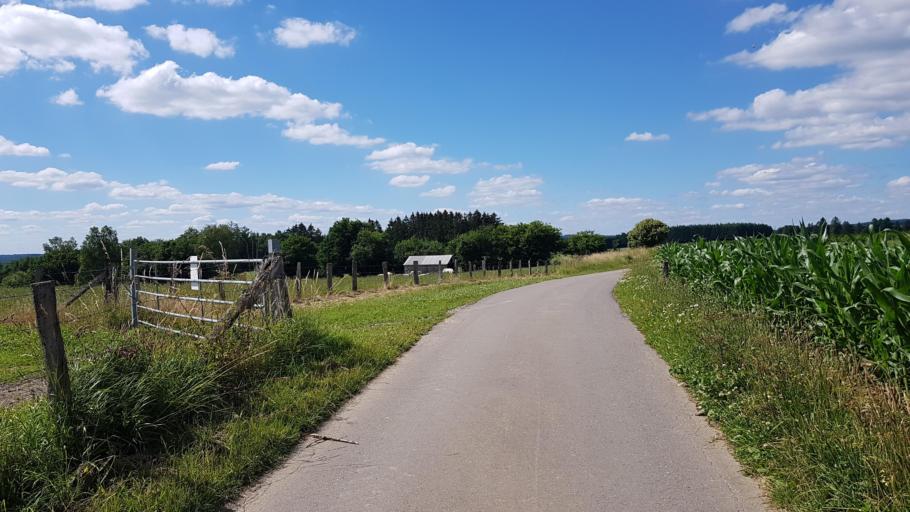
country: BE
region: Wallonia
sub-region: Province du Luxembourg
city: Bouillon
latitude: 49.8058
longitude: 5.0625
